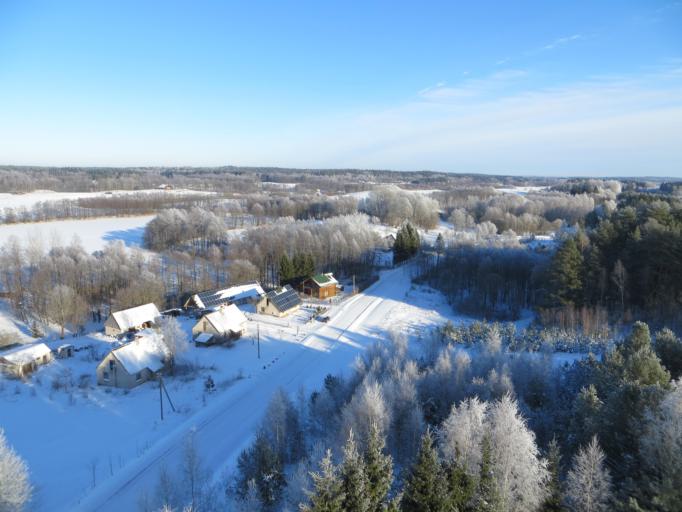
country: LT
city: Zarasai
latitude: 55.6176
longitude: 26.1071
